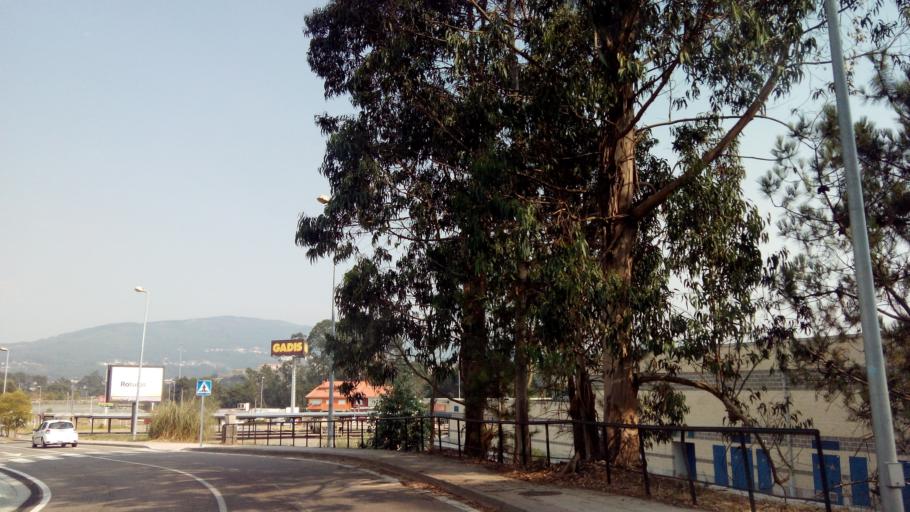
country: PT
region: Viana do Castelo
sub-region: Valenca
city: Valenca
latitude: 42.0372
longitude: -8.6614
